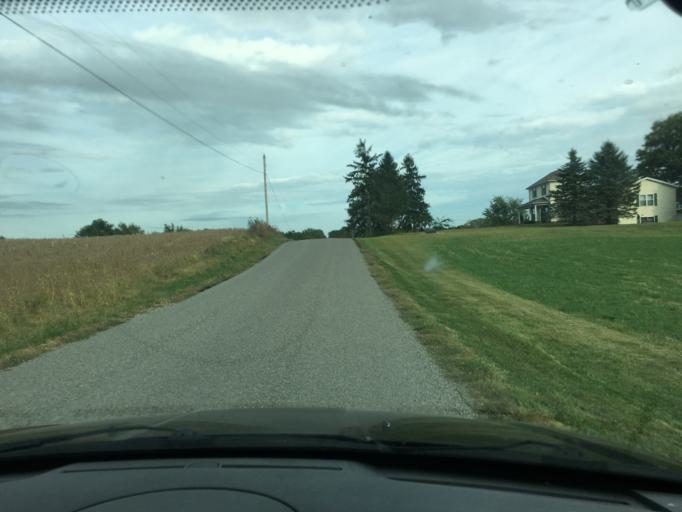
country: US
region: Ohio
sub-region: Logan County
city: Bellefontaine
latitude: 40.3188
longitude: -83.7846
